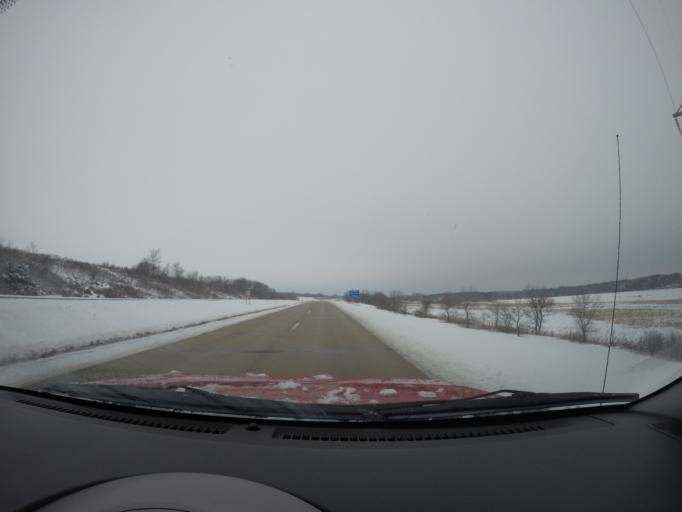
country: US
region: Minnesota
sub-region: Olmsted County
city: Rochester
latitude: 43.9553
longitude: -92.3689
